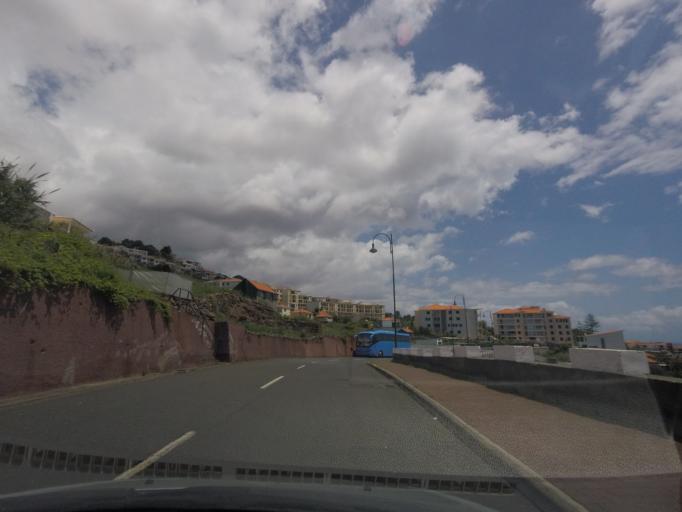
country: PT
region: Madeira
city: Canico
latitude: 32.6455
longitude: -16.8386
